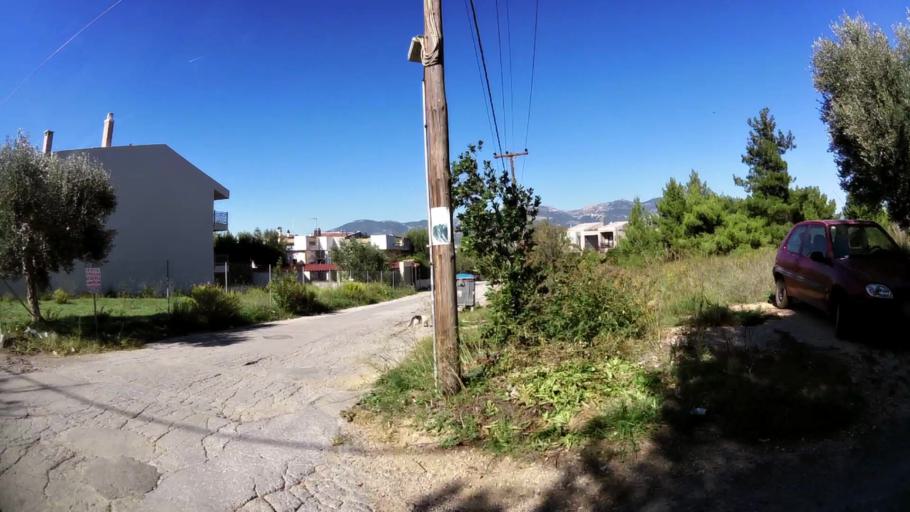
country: GR
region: Attica
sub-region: Nomarchia Athinas
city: Lykovrysi
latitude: 38.0946
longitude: 23.7870
